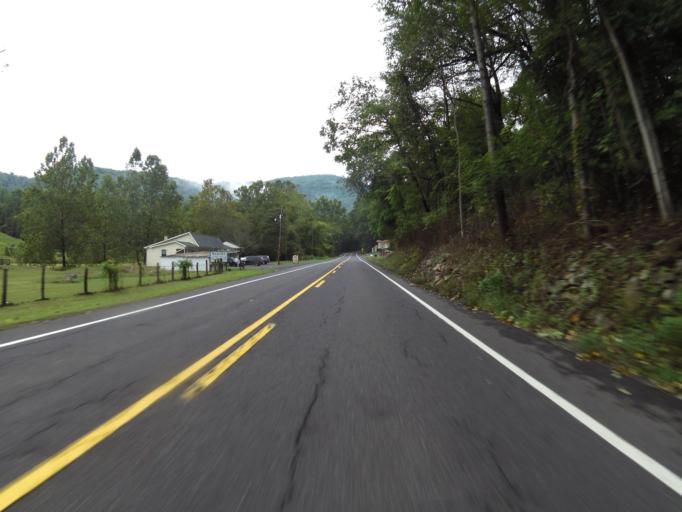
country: US
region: Virginia
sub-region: Rappahannock County
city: Washington
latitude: 38.6515
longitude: -78.2546
